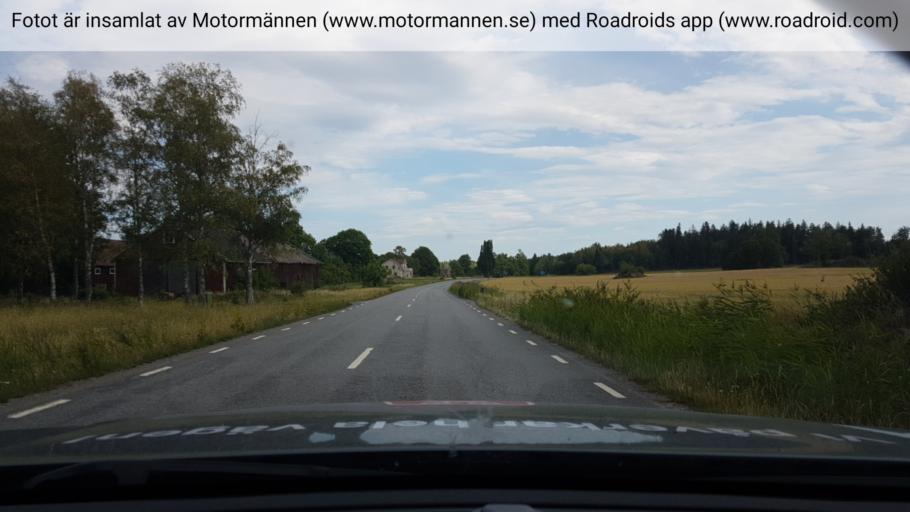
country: SE
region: Uppsala
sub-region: Enkopings Kommun
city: Grillby
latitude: 59.6437
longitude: 17.2658
